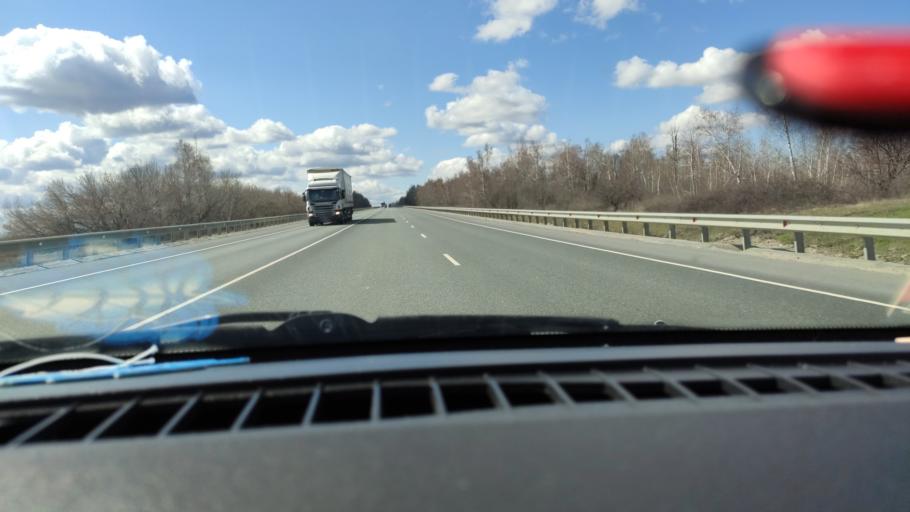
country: RU
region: Saratov
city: Khvalynsk
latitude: 52.5622
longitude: 48.0902
